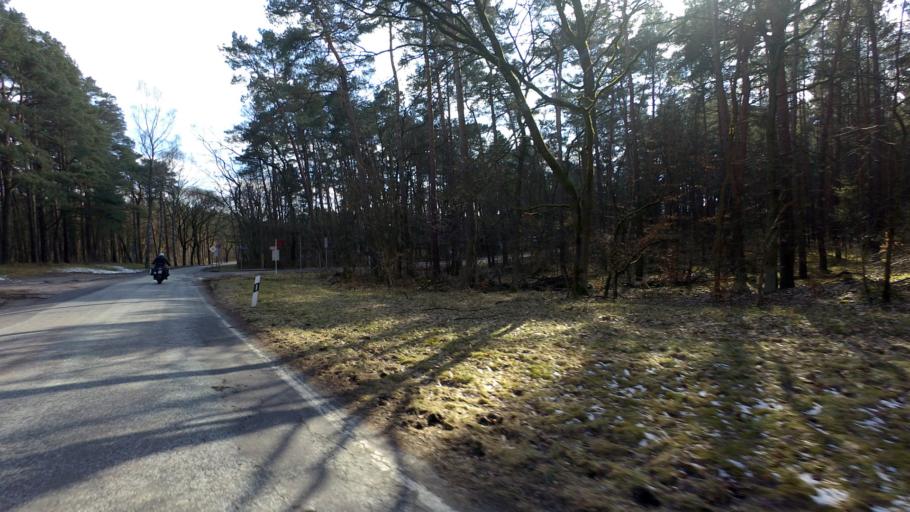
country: DE
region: Brandenburg
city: Biesenthal
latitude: 52.7791
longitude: 13.6142
